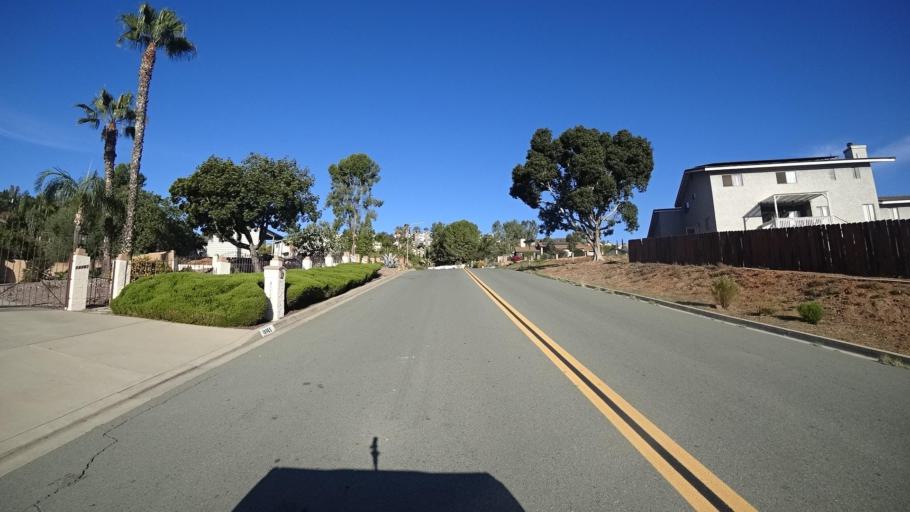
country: US
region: California
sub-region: San Diego County
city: La Presa
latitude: 32.7185
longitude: -116.9806
